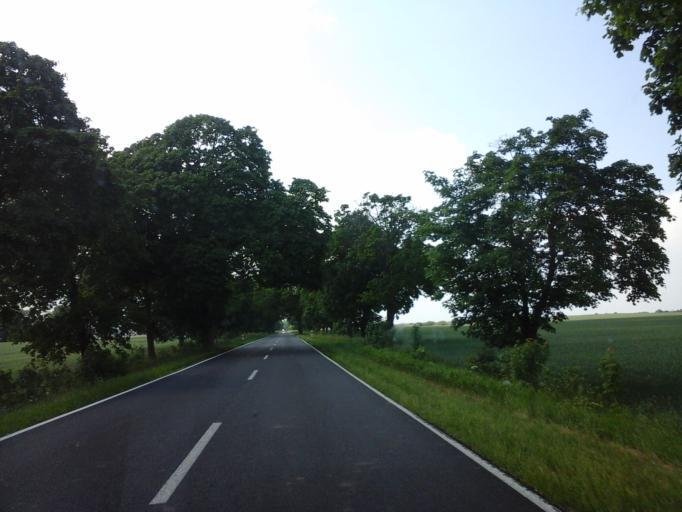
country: PL
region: West Pomeranian Voivodeship
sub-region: Powiat choszczenski
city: Recz
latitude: 53.1895
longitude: 15.6107
